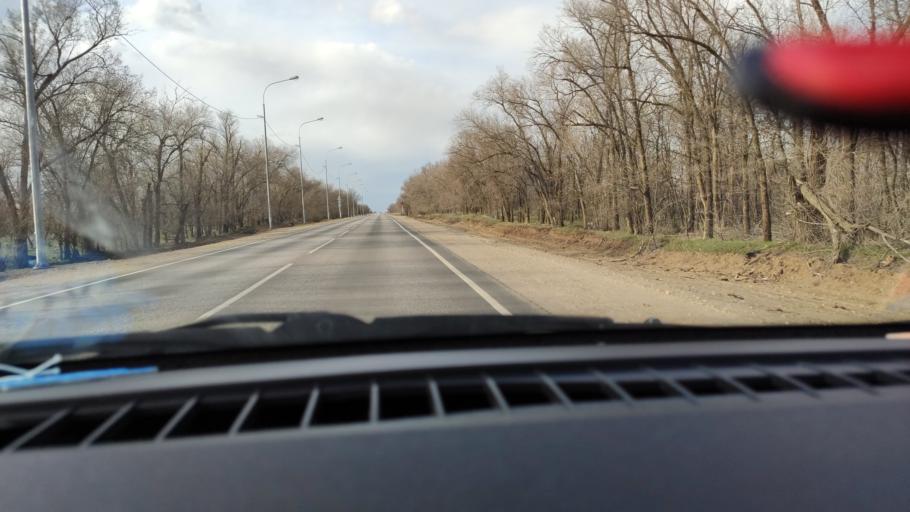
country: RU
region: Saratov
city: Krasnoarmeysk
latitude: 51.0948
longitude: 45.9556
